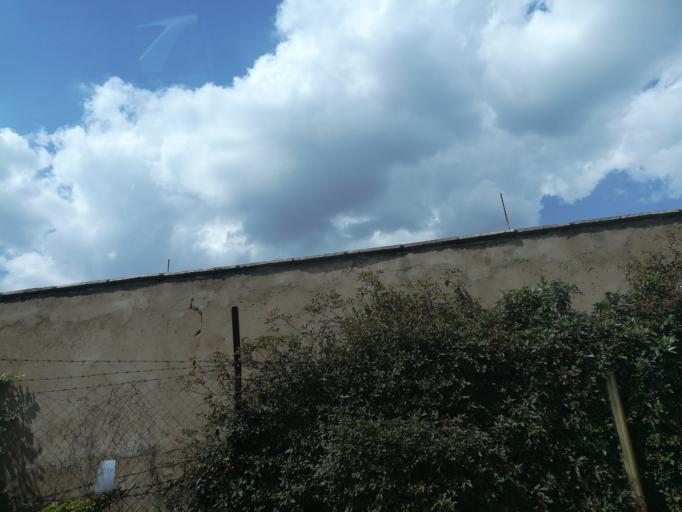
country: KE
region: Nairobi Area
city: Nairobi
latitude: -1.3246
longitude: 36.8035
